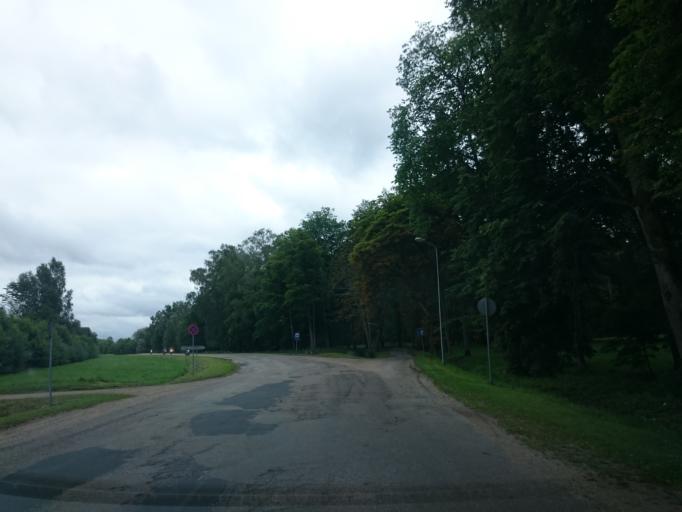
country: LV
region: Pavilostas
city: Pavilosta
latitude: 56.8796
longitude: 21.2120
